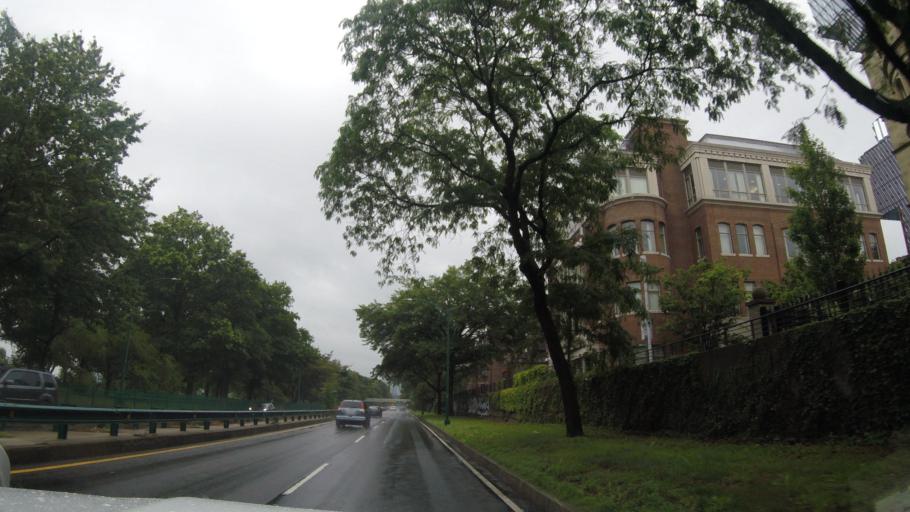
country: US
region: Massachusetts
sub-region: Middlesex County
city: Cambridge
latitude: 42.3509
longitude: -71.1037
